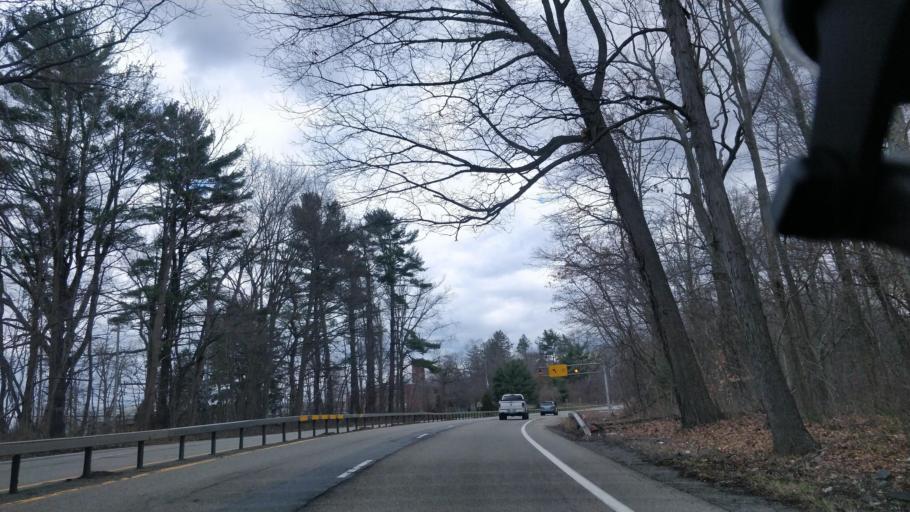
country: US
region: New York
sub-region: Westchester County
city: Ossining
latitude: 41.1769
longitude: -73.8400
